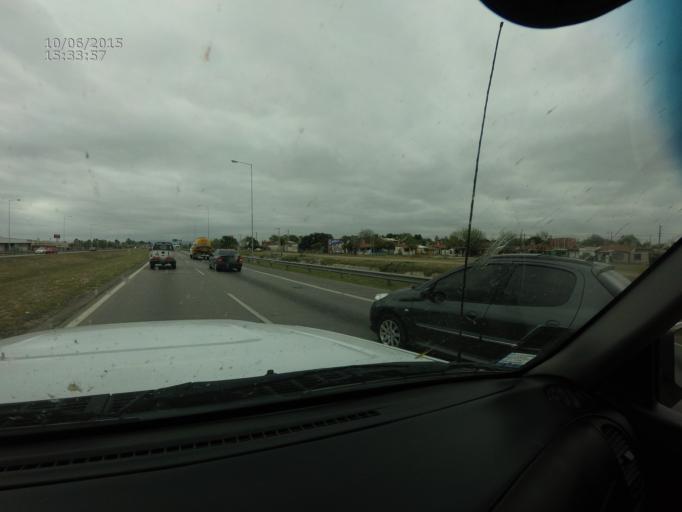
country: AR
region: Cordoba
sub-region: Departamento de Capital
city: Cordoba
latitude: -31.3587
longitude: -64.1690
